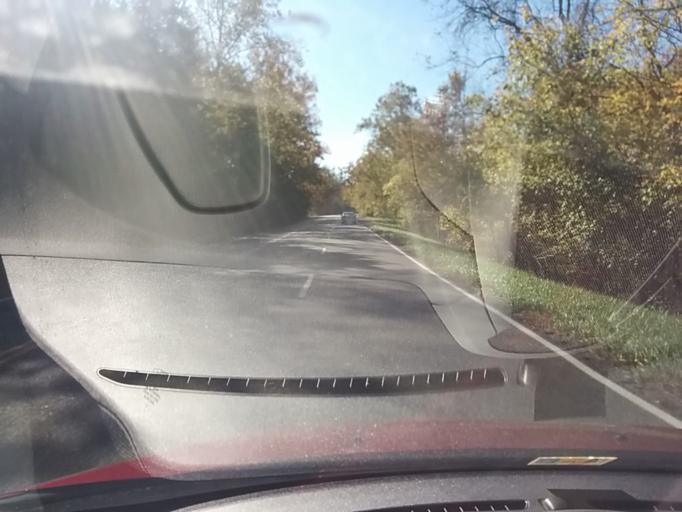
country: US
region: Virginia
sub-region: City of Lexington
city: Lexington
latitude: 37.7659
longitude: -79.4471
